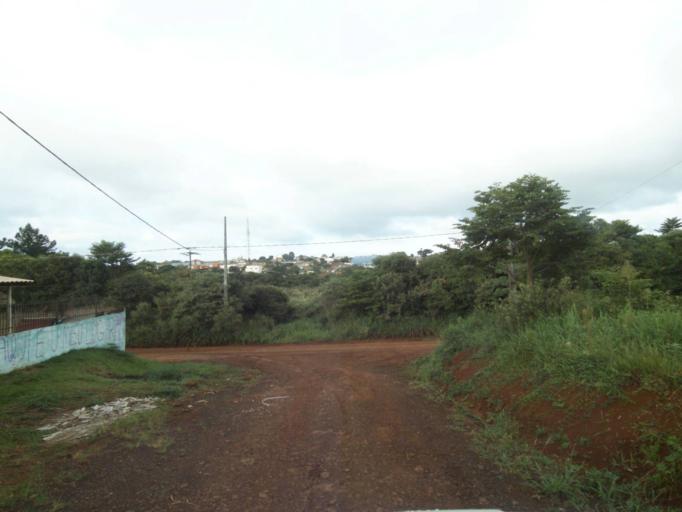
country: BR
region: Parana
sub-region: Pitanga
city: Pitanga
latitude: -24.9384
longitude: -51.8663
